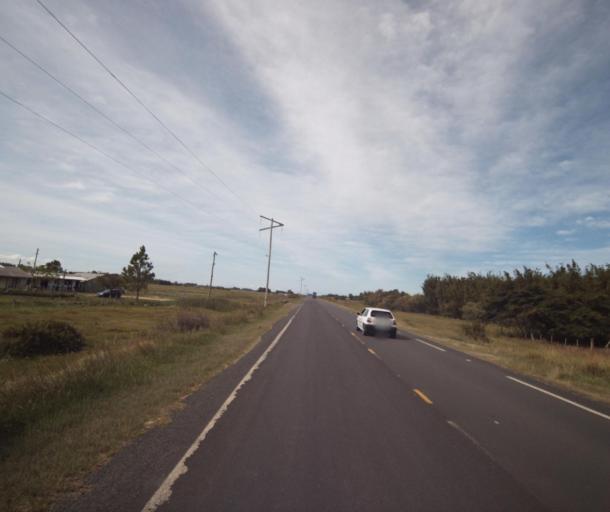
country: BR
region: Rio Grande do Sul
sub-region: Rio Grande
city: Rio Grande
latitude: -31.9456
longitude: -51.9775
